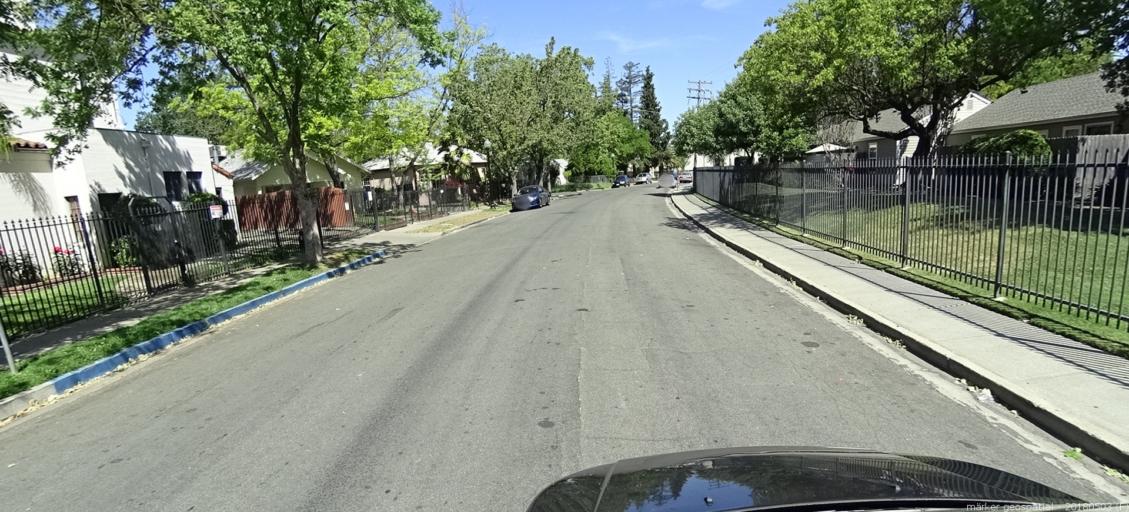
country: US
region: California
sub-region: Sacramento County
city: Sacramento
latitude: 38.6087
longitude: -121.4571
